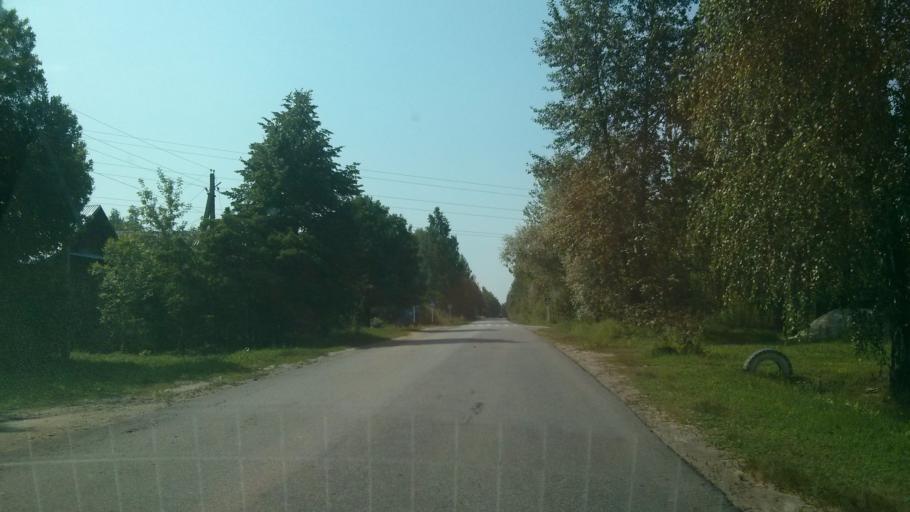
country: RU
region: Vladimir
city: Murom
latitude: 55.5324
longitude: 42.0236
